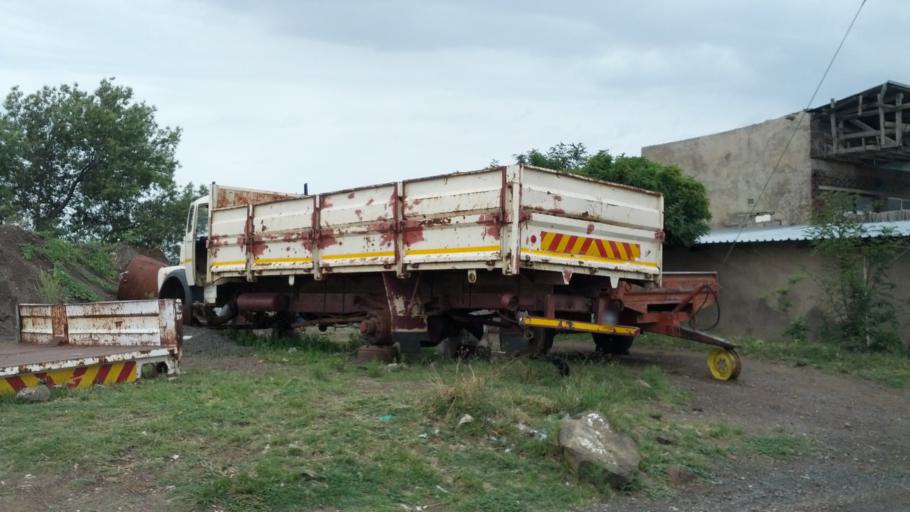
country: LS
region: Berea
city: Teyateyaneng
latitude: -29.1021
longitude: 27.9593
